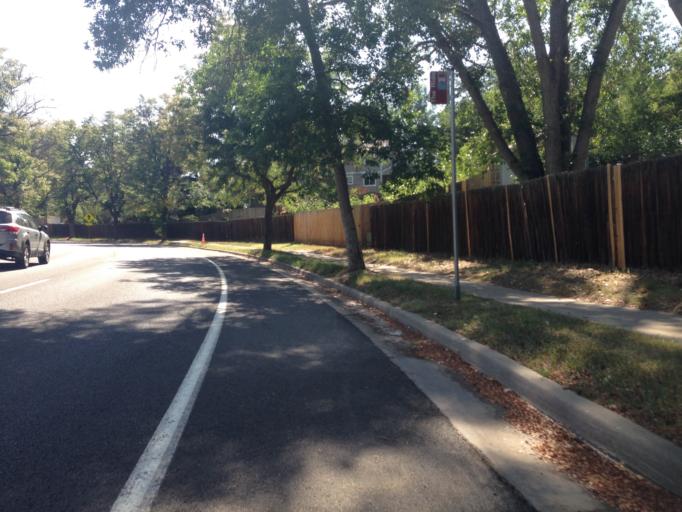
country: US
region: Colorado
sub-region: Boulder County
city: Louisville
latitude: 39.9845
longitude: -105.1439
